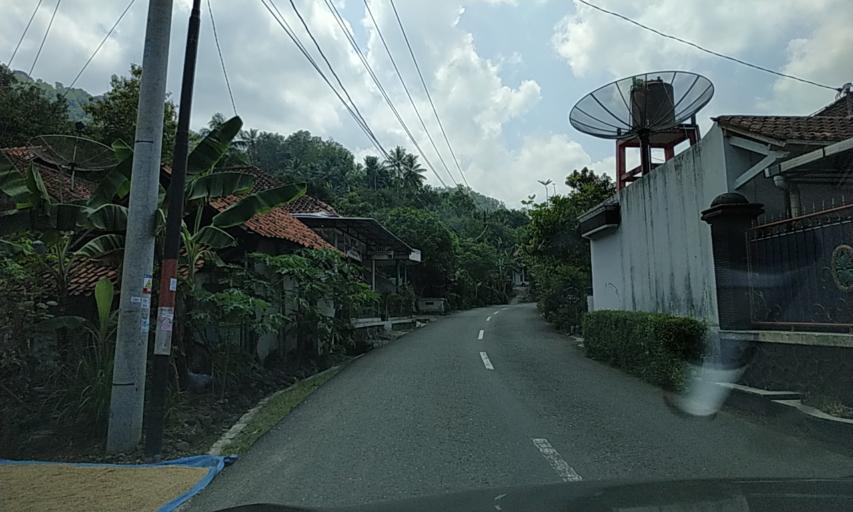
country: ID
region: Central Java
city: Gombong
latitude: -7.6296
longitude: 109.7168
